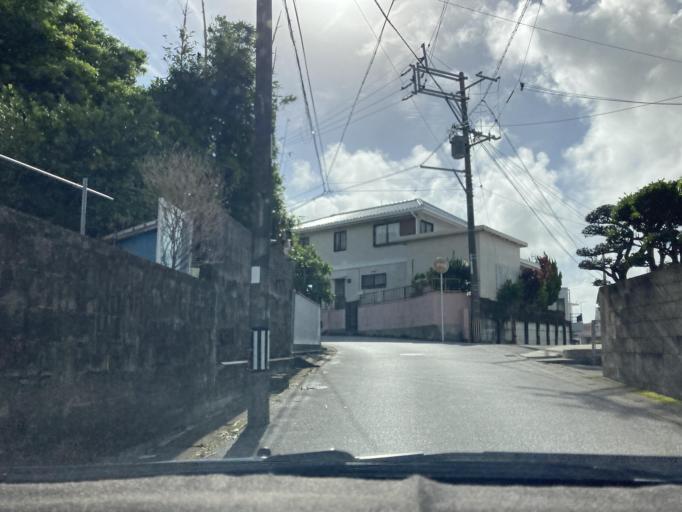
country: JP
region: Okinawa
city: Naha-shi
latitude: 26.2026
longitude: 127.7296
